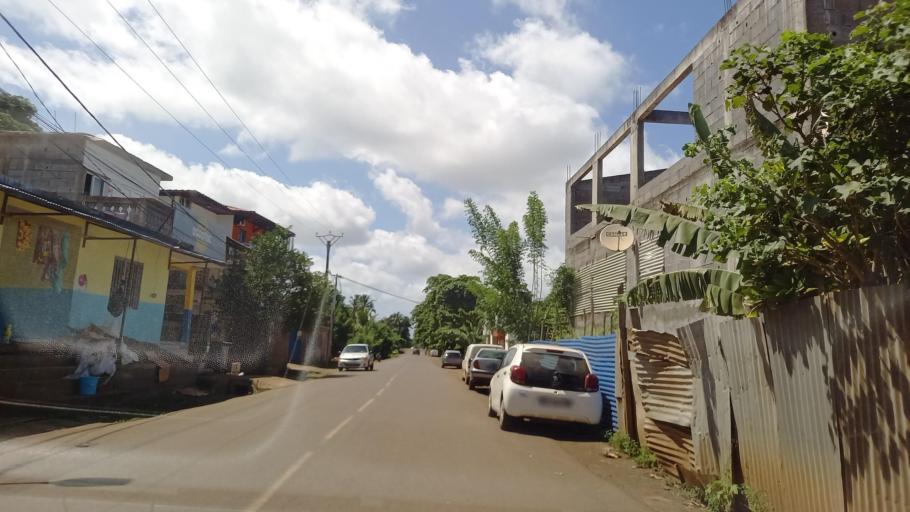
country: YT
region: Bandraboua
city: Bandraboua
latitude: -12.7223
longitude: 45.1216
